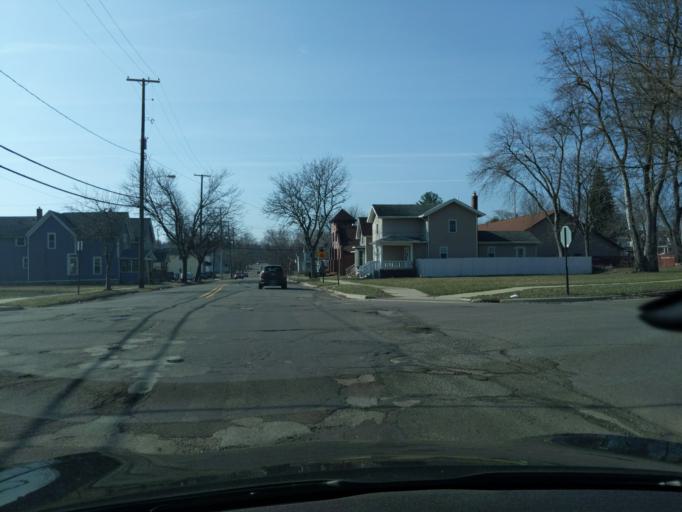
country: US
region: Michigan
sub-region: Jackson County
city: Jackson
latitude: 42.2448
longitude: -84.4118
